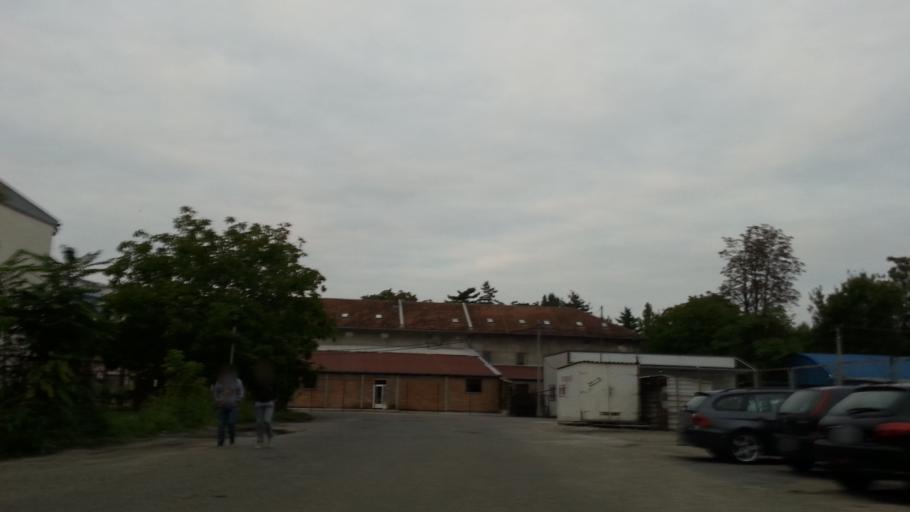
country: RS
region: Central Serbia
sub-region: Belgrade
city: Zemun
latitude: 44.8124
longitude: 20.3930
